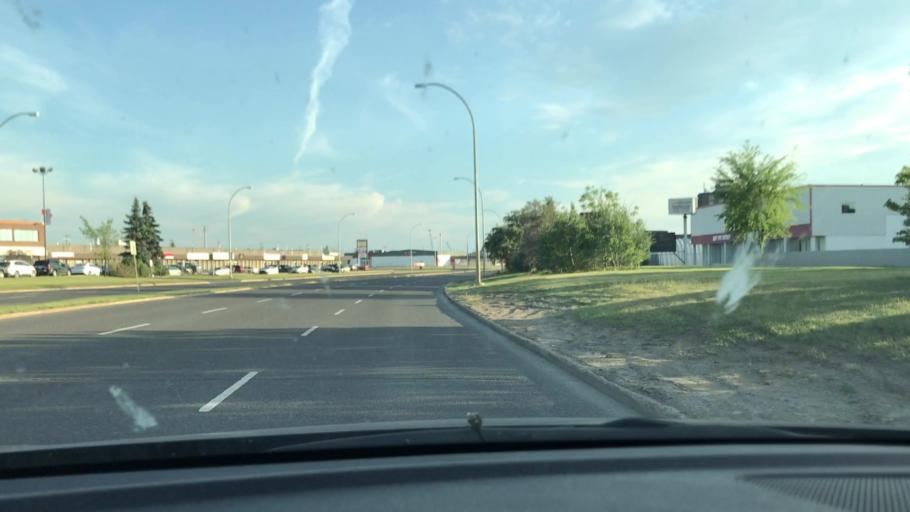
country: CA
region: Alberta
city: Edmonton
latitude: 53.5117
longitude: -113.4374
